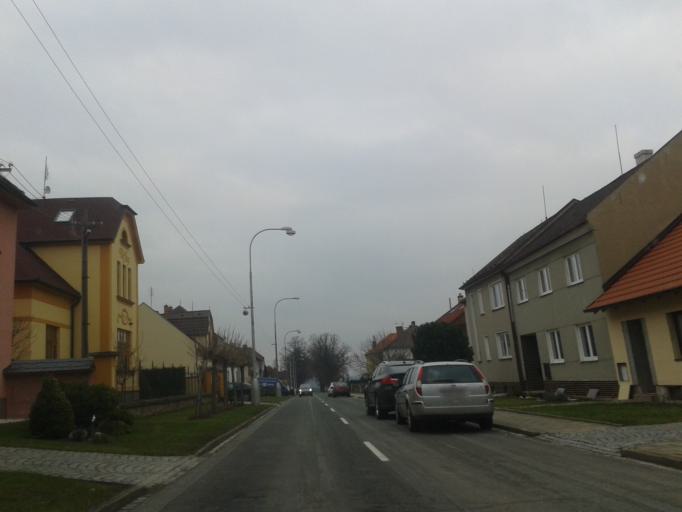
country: CZ
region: Olomoucky
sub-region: Okres Olomouc
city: Slatinice
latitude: 49.5658
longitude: 17.1042
